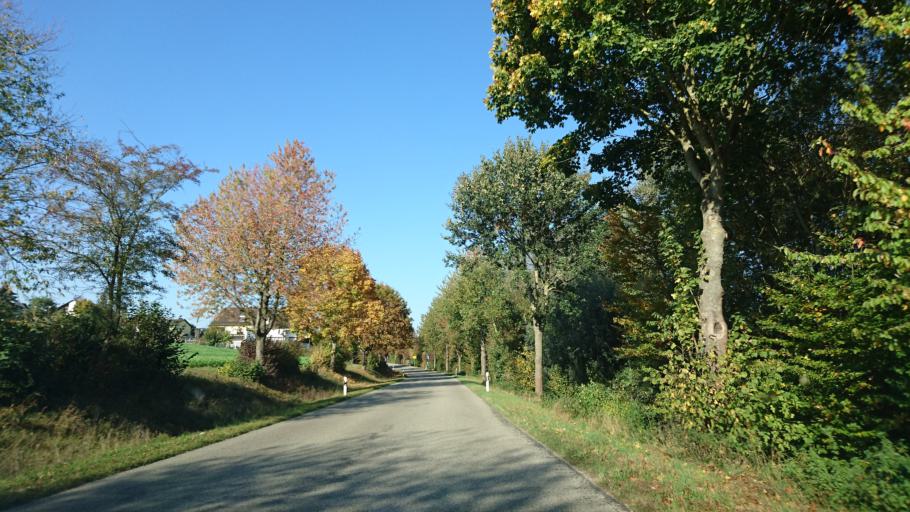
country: DE
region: Bavaria
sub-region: Swabia
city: Zusmarshausen
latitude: 48.4118
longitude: 10.5873
